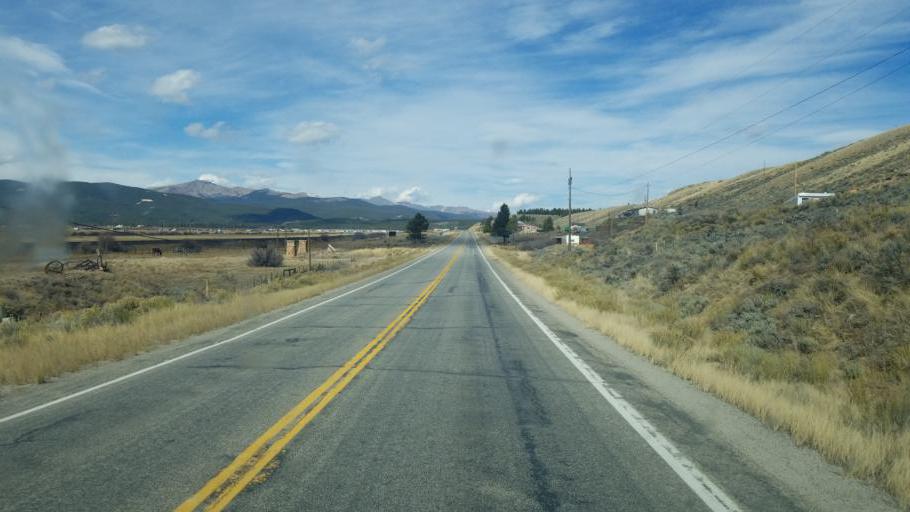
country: US
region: Colorado
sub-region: Lake County
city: Leadville North
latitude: 39.2076
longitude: -106.3451
